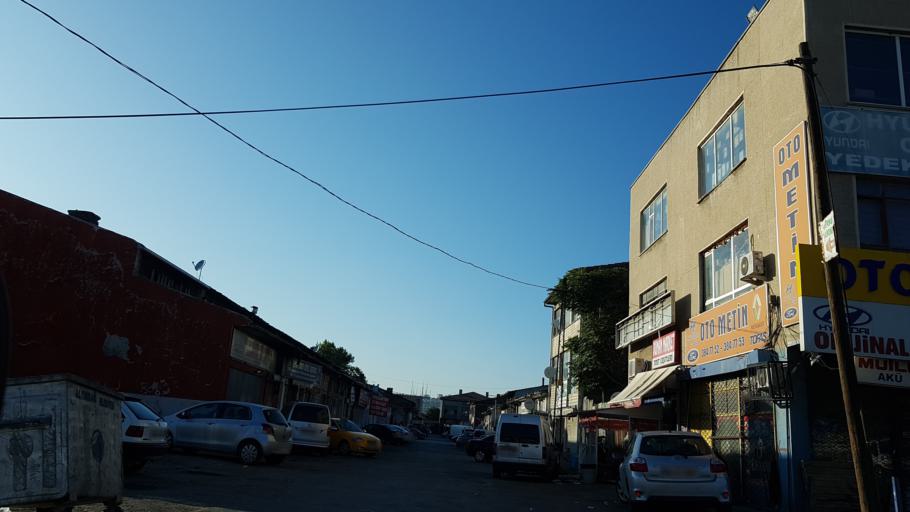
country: TR
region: Ankara
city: Ankara
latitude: 39.9484
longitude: 32.8437
